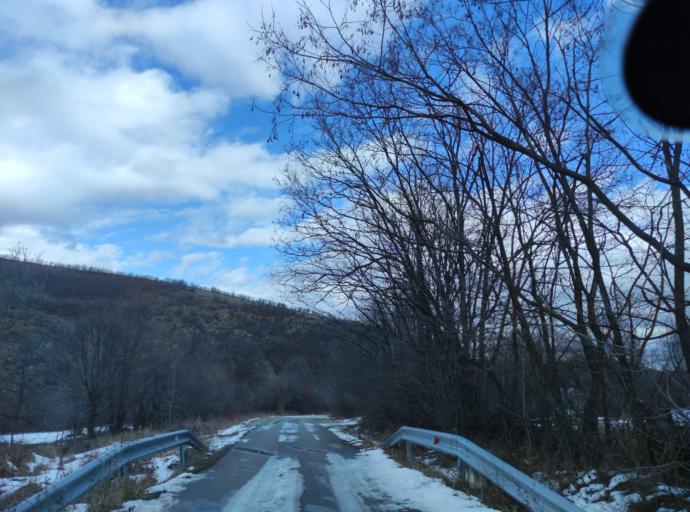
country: BG
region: Montana
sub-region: Obshtina Chiprovtsi
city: Chiprovtsi
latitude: 43.3781
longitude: 22.8577
